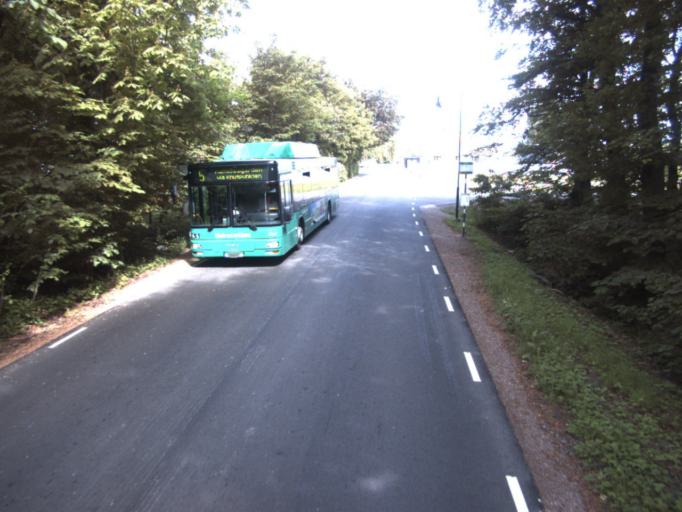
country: SE
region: Skane
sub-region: Helsingborg
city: Odakra
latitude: 56.0891
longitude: 12.6981
